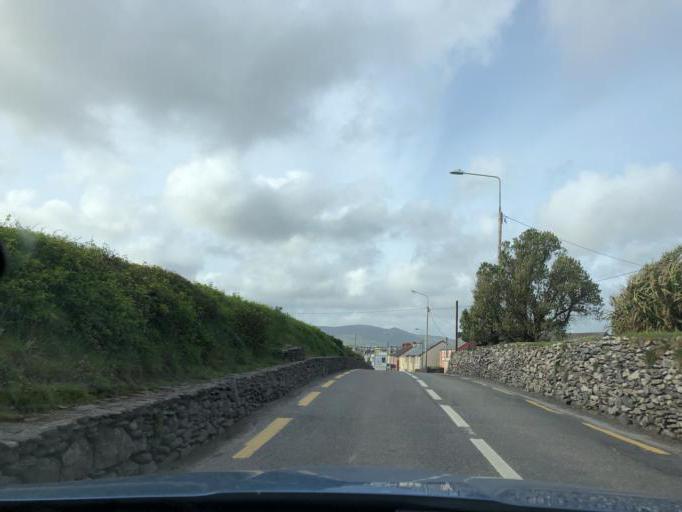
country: IE
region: Munster
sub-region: Ciarrai
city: Cahersiveen
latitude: 51.8218
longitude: -10.1719
